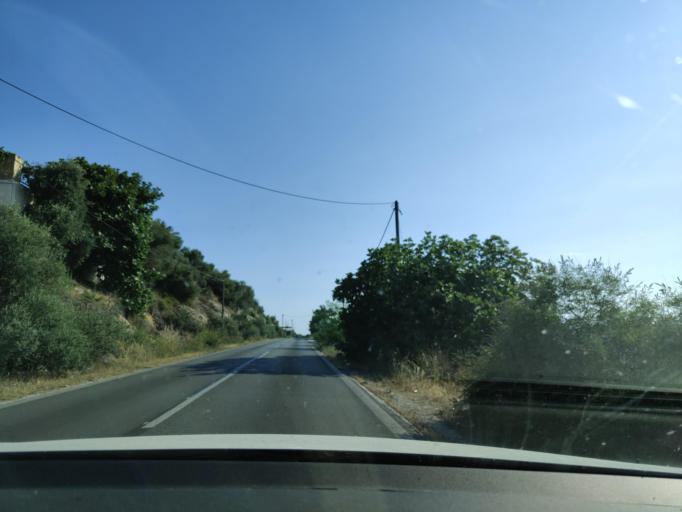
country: GR
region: East Macedonia and Thrace
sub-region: Nomos Kavalas
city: Prinos
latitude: 40.7165
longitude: 24.5370
